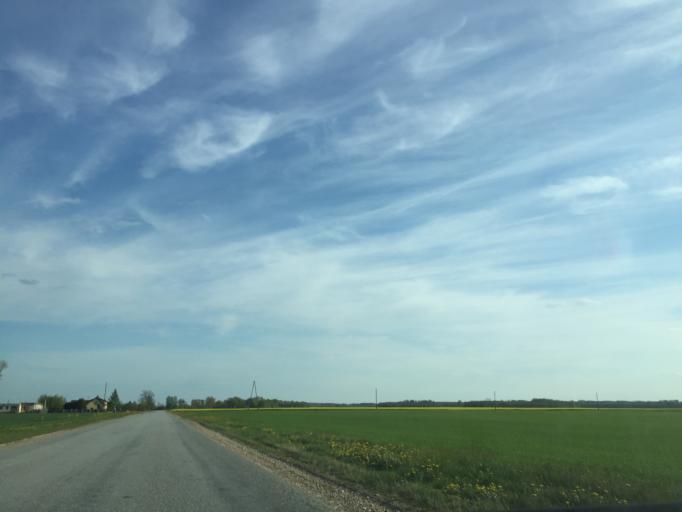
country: LV
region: Bauskas Rajons
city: Bauska
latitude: 56.3670
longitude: 24.2289
